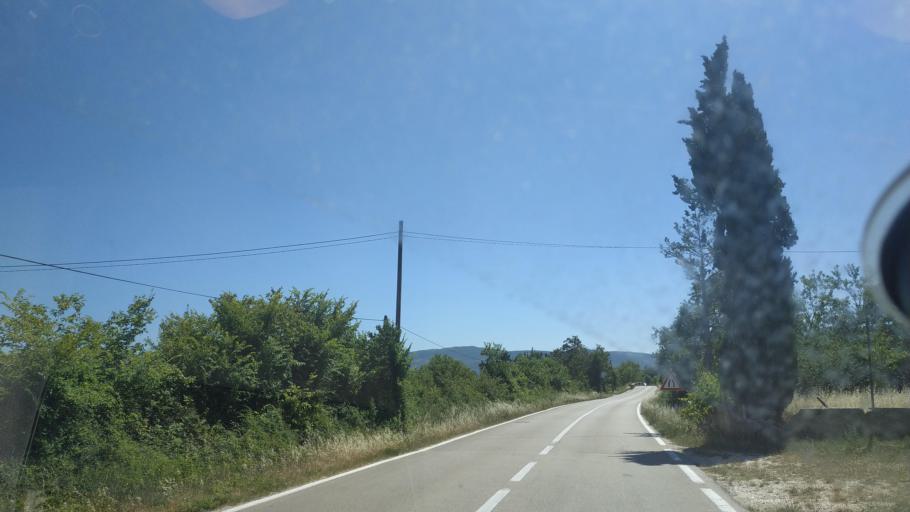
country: HR
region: Sibensko-Kniniska
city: Drnis
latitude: 43.8873
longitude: 16.2076
